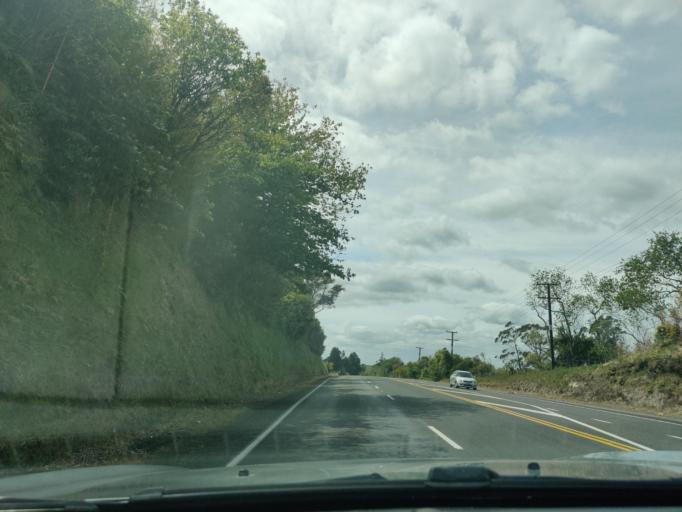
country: NZ
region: Taranaki
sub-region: New Plymouth District
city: New Plymouth
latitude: -39.1509
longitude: 174.1670
